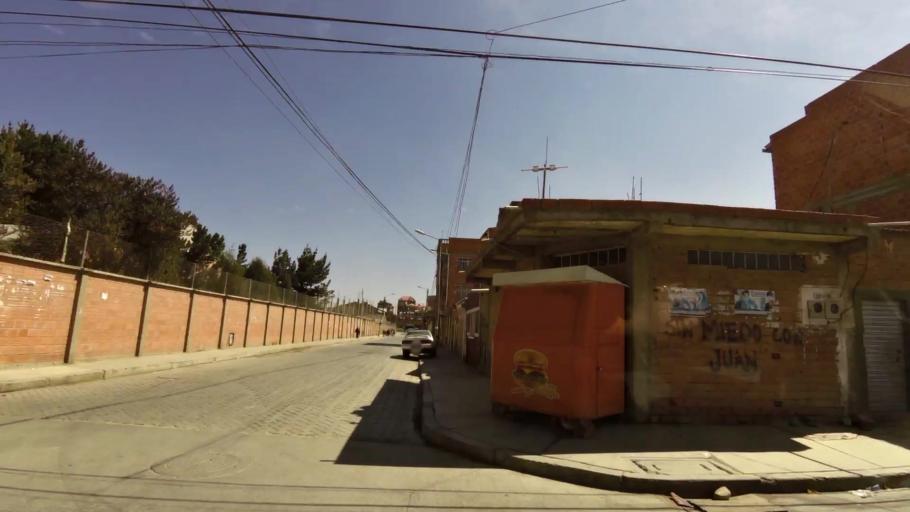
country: BO
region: La Paz
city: La Paz
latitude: -16.5280
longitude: -68.1584
